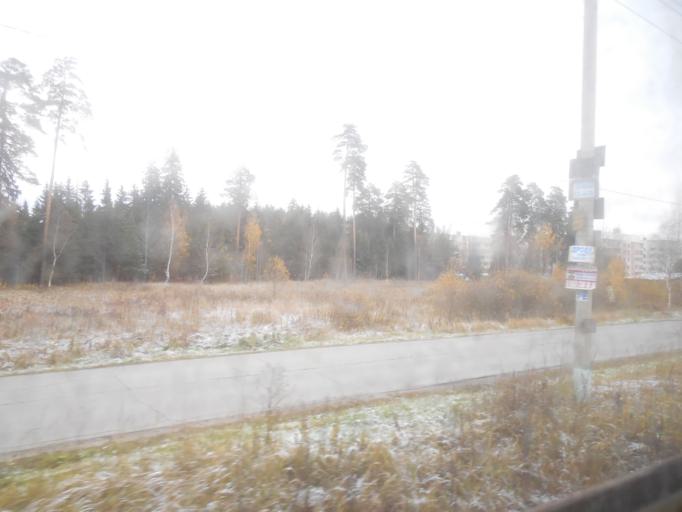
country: RU
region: Moskovskaya
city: Bol'shiye Vyazemy
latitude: 55.6715
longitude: 36.9499
